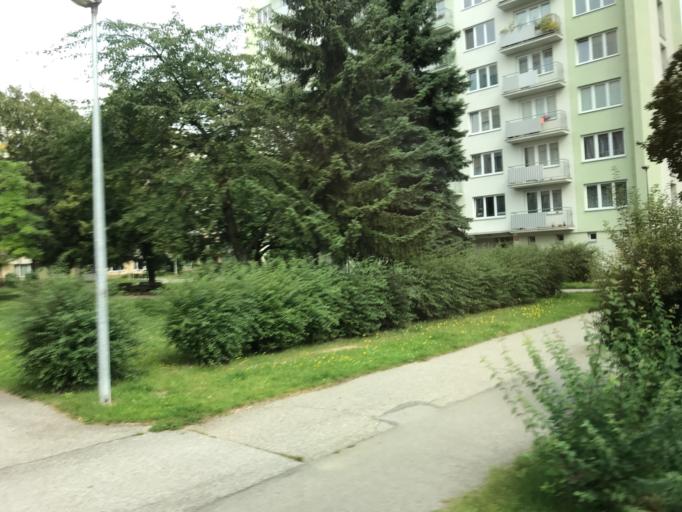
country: CZ
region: Jihocesky
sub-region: Okres Ceske Budejovice
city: Ceske Budejovice
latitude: 48.9681
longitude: 14.4746
